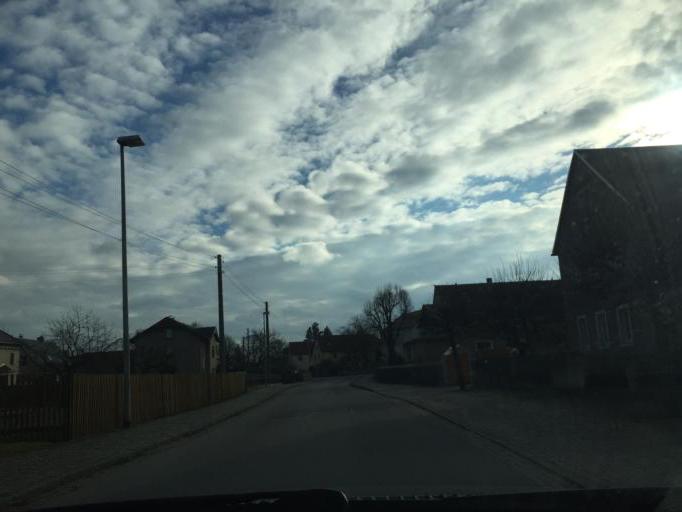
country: DE
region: Saxony
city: Ebersbach
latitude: 51.2419
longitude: 13.6601
